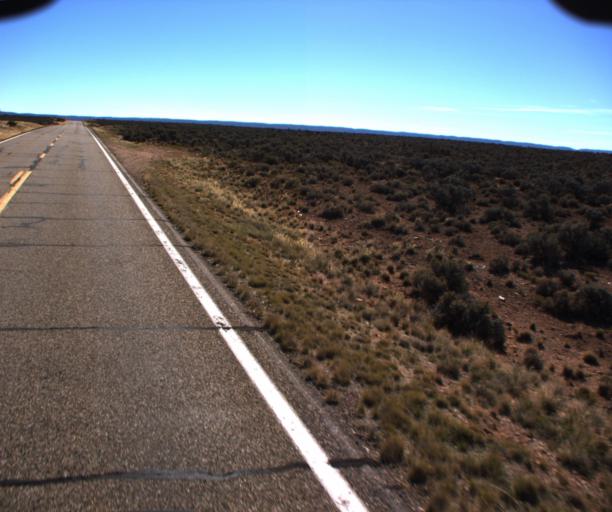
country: US
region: Arizona
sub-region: Coconino County
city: Fredonia
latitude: 36.8984
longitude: -112.3715
